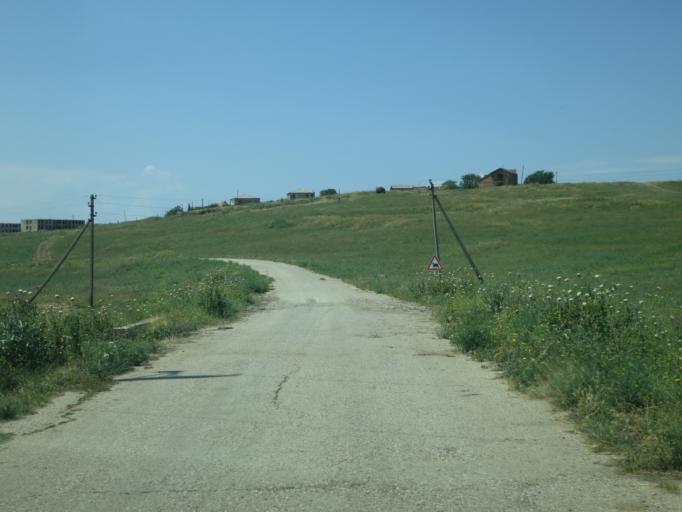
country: GE
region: Kakheti
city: Sagarejo
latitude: 41.5072
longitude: 45.3853
